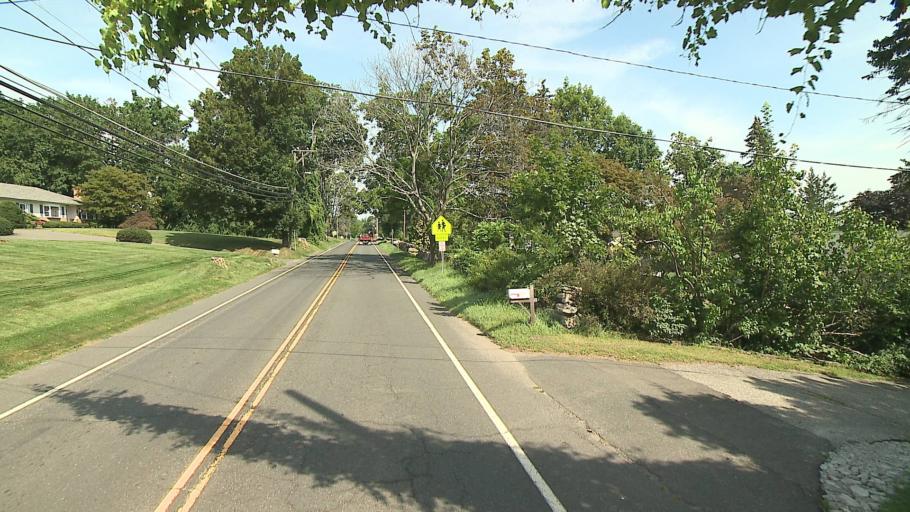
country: US
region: Connecticut
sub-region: Fairfield County
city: Danbury
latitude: 41.4139
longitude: -73.4710
